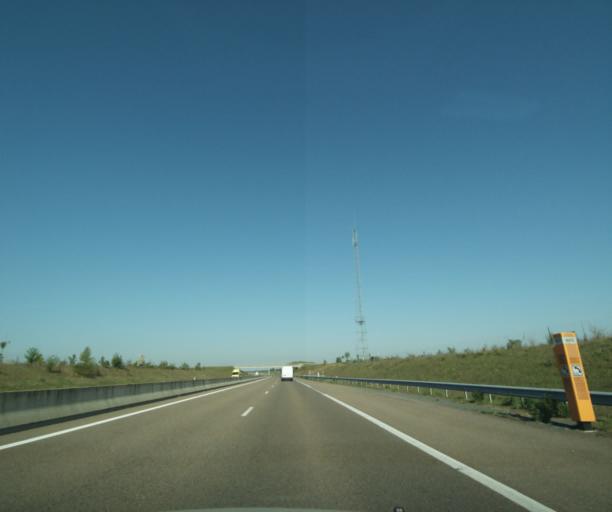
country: FR
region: Centre
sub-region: Departement du Loiret
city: Boynes
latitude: 48.1056
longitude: 2.3235
